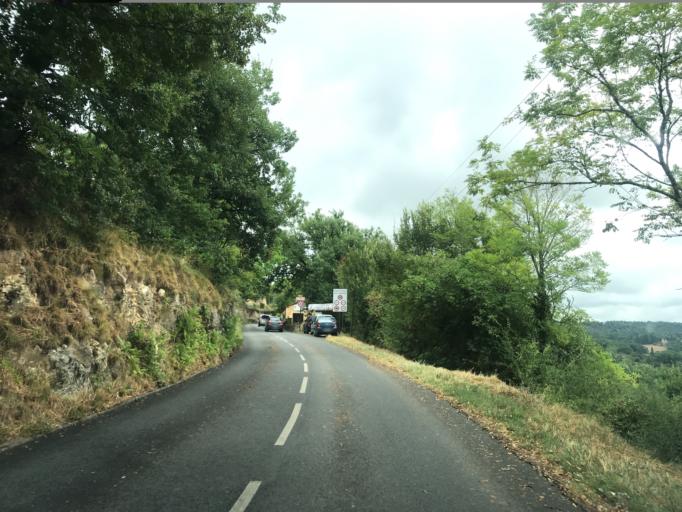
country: FR
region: Aquitaine
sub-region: Departement de la Dordogne
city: Cenac-et-Saint-Julien
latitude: 44.8019
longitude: 1.2096
